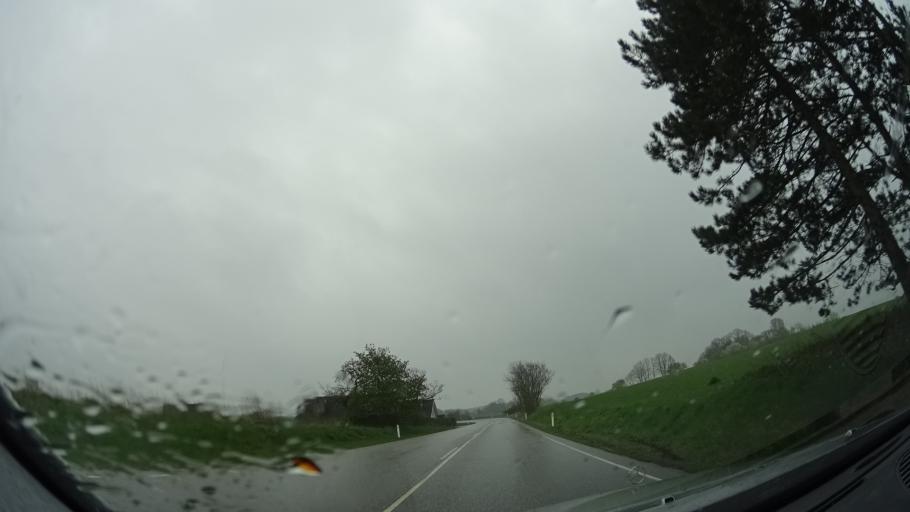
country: DK
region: Zealand
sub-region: Odsherred Kommune
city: Asnaes
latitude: 55.8259
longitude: 11.5729
